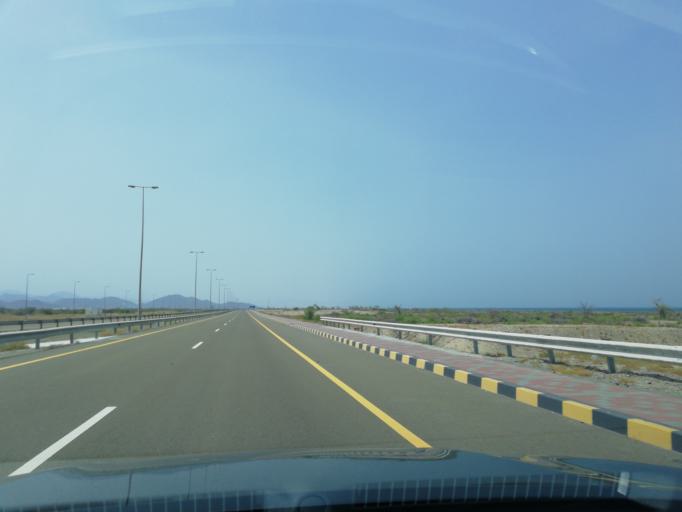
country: OM
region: Al Batinah
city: Shinas
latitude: 24.9091
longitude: 56.3927
